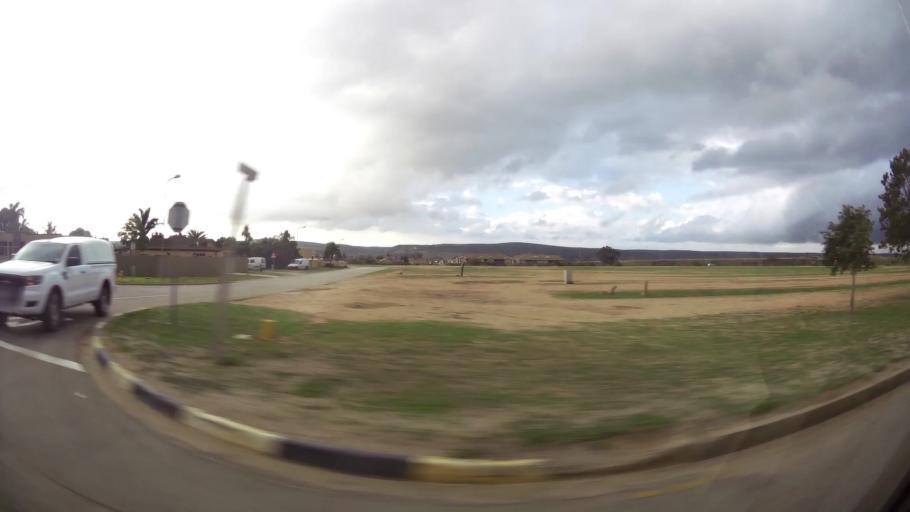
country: ZA
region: Eastern Cape
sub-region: Nelson Mandela Bay Metropolitan Municipality
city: Uitenhage
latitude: -33.8066
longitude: 25.4905
